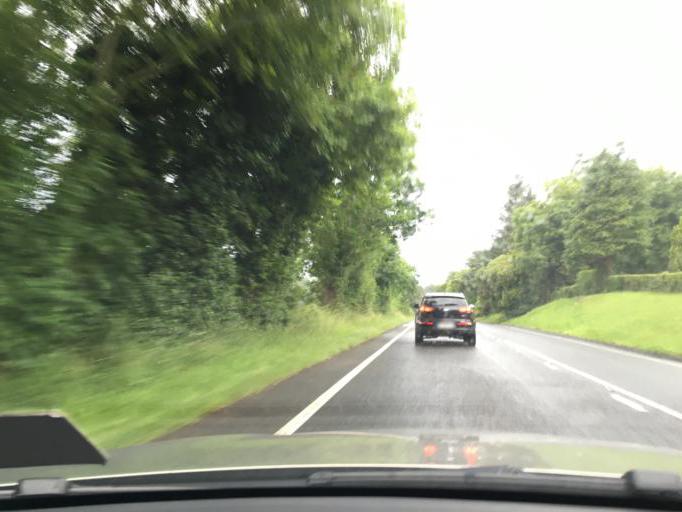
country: GB
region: Northern Ireland
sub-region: Fermanagh District
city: Enniskillen
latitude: 54.3810
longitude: -7.6369
